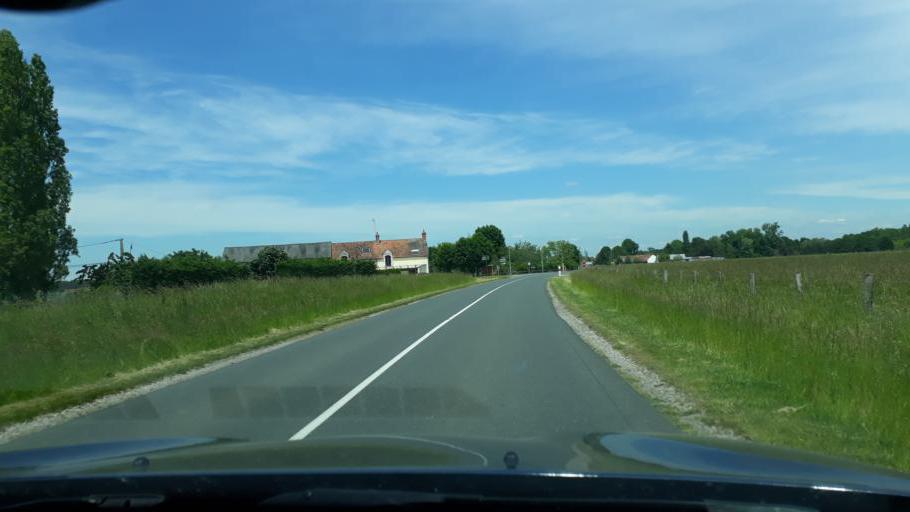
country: FR
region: Centre
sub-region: Departement du Loiret
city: Boiscommun
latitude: 48.0504
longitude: 2.2984
